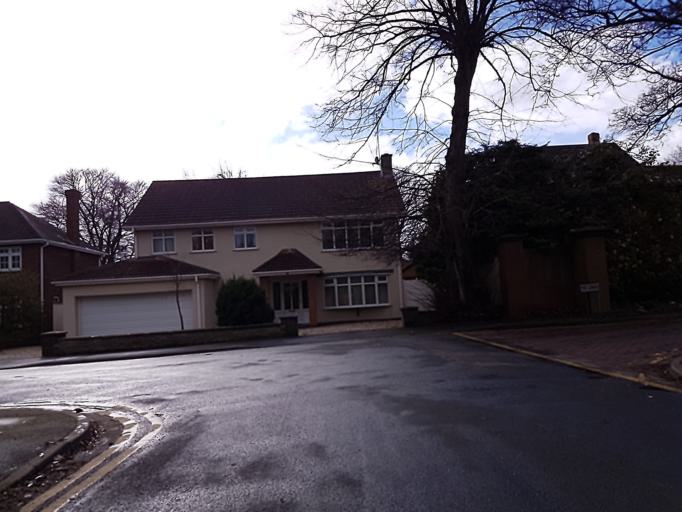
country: GB
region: England
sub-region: North East Lincolnshire
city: Grimbsy
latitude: 53.5626
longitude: -0.0941
